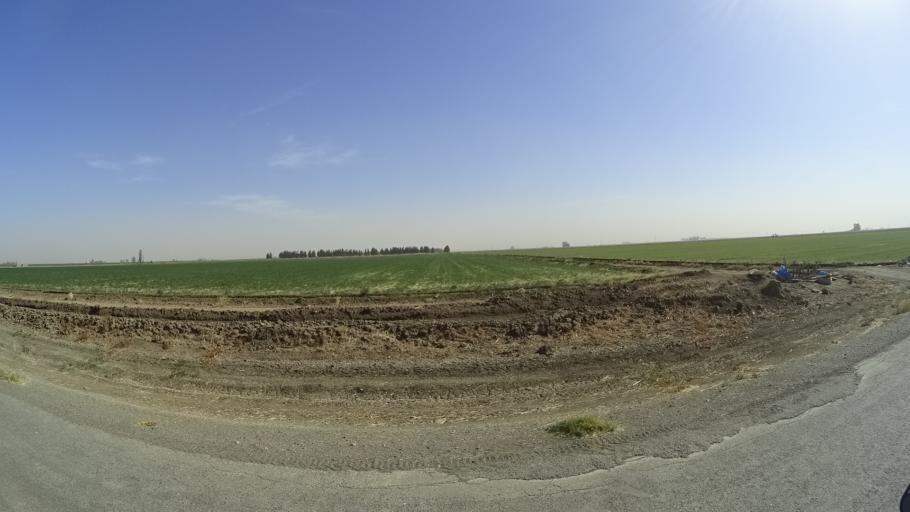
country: US
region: California
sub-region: Yolo County
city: Davis
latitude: 38.4633
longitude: -121.6937
